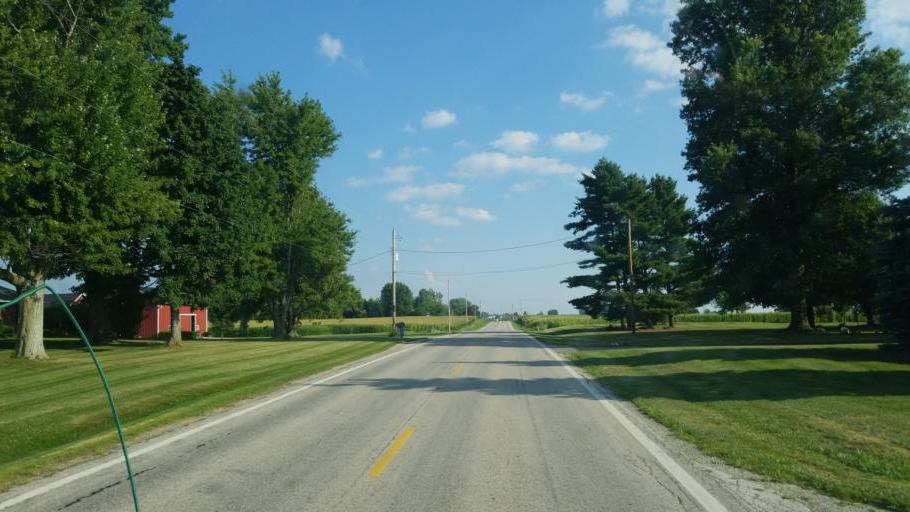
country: US
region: Ohio
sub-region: Crawford County
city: Bucyrus
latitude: 40.8809
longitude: -83.0098
